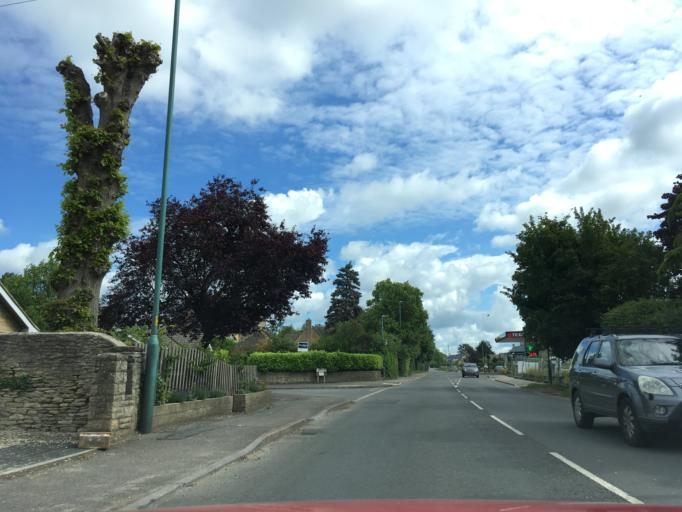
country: GB
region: England
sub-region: Gloucestershire
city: Lechlade
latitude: 51.7005
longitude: -1.6889
